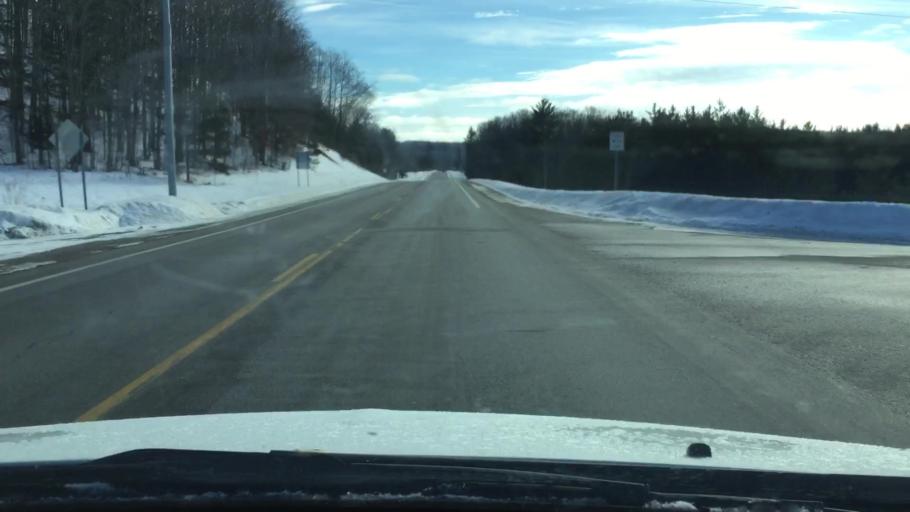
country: US
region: Michigan
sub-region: Antrim County
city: Mancelona
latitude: 44.9677
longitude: -85.0539
